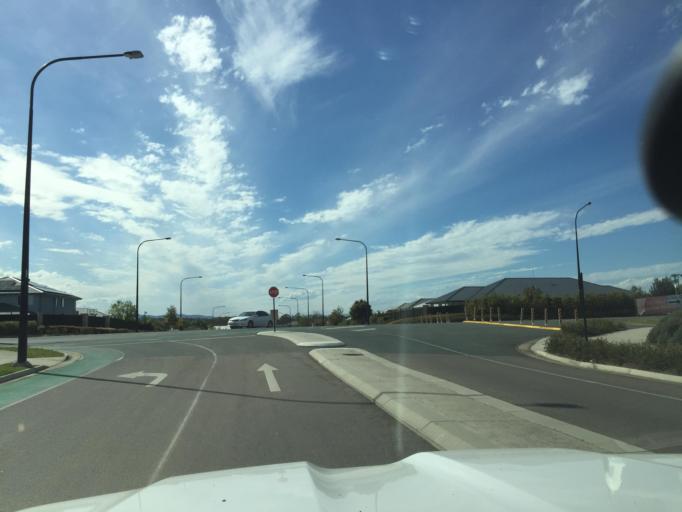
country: AU
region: Queensland
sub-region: Moreton Bay
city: Morayfield
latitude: -27.1215
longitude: 152.9967
